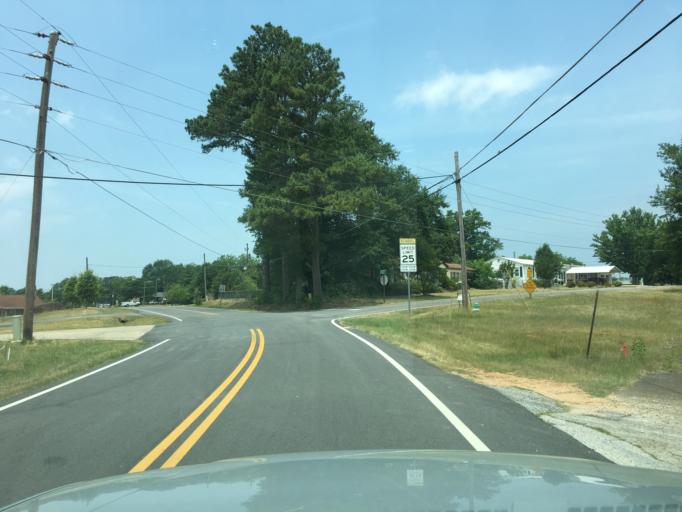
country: US
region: Georgia
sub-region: Hart County
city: Hartwell
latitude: 34.3497
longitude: -82.9171
